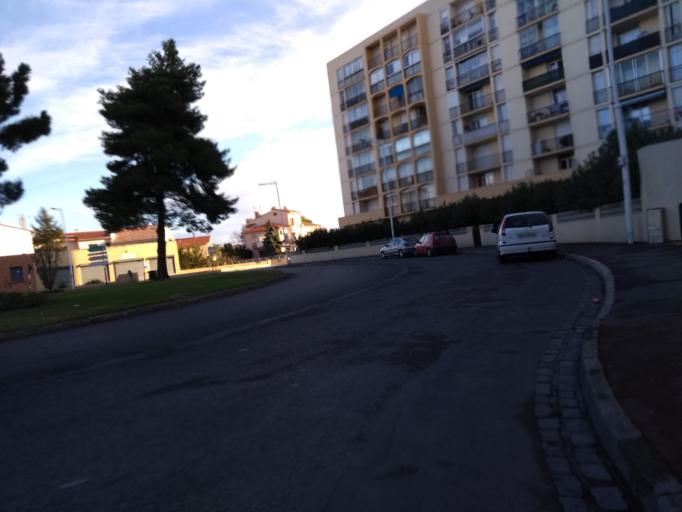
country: FR
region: Languedoc-Roussillon
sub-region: Departement des Pyrenees-Orientales
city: Perpignan
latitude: 42.7156
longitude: 2.8883
